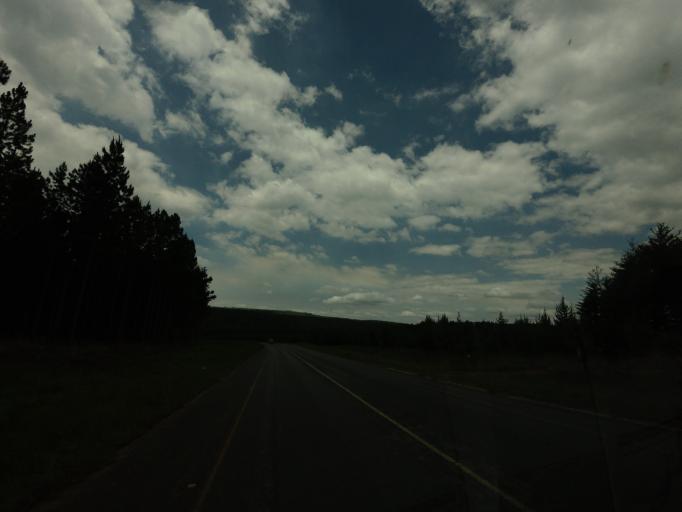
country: ZA
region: Mpumalanga
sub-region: Ehlanzeni District
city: Graksop
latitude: -24.9689
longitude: 30.8085
